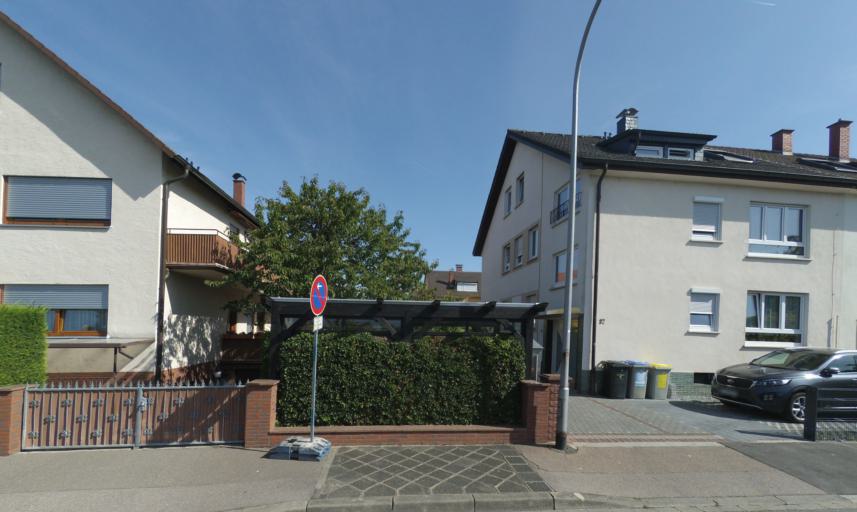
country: DE
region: Hesse
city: Lampertheim
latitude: 49.5585
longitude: 8.4793
